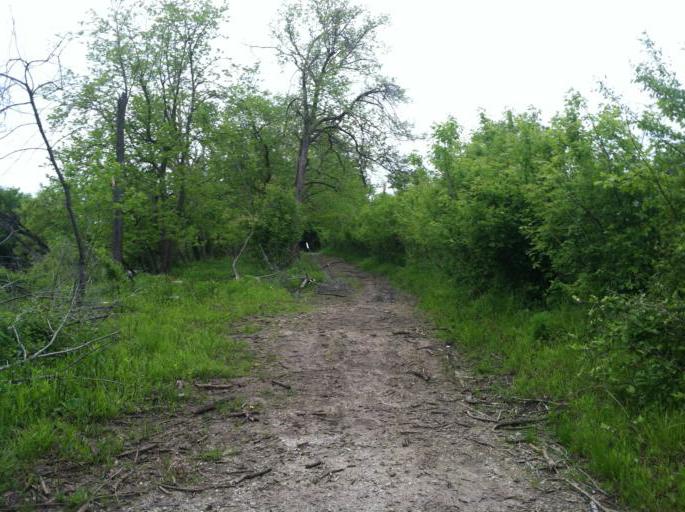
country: US
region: Illinois
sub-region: Cook County
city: River Grove
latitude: 41.9360
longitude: -87.8481
